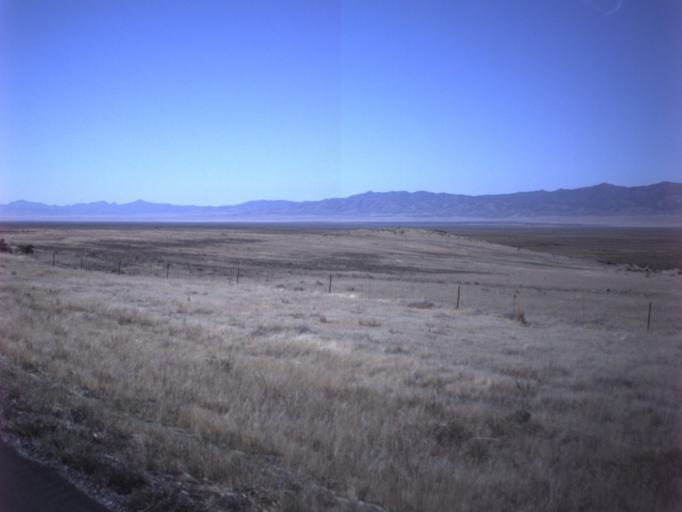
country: US
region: Utah
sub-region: Tooele County
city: Grantsville
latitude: 40.5685
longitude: -112.7316
